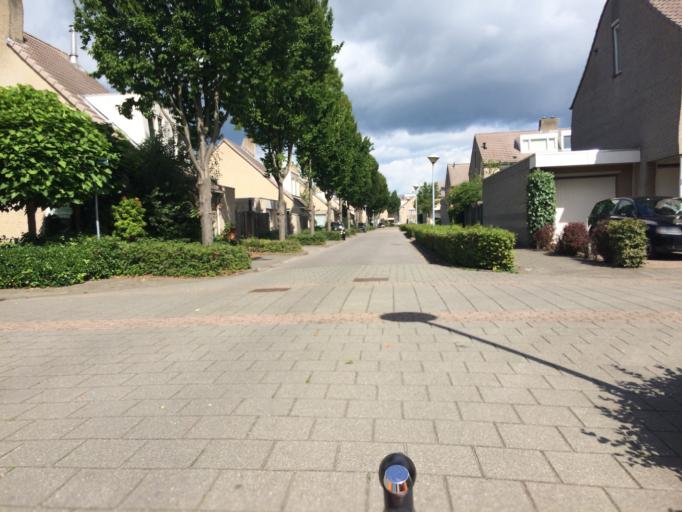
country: NL
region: Gelderland
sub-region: Gemeente Maasdriel
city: Hedel
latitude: 51.7282
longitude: 5.2868
